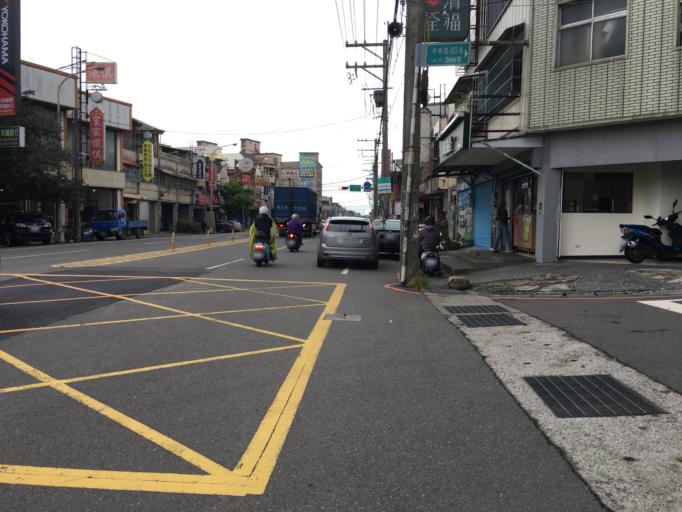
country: TW
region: Taiwan
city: Daxi
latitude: 24.8722
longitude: 121.2280
